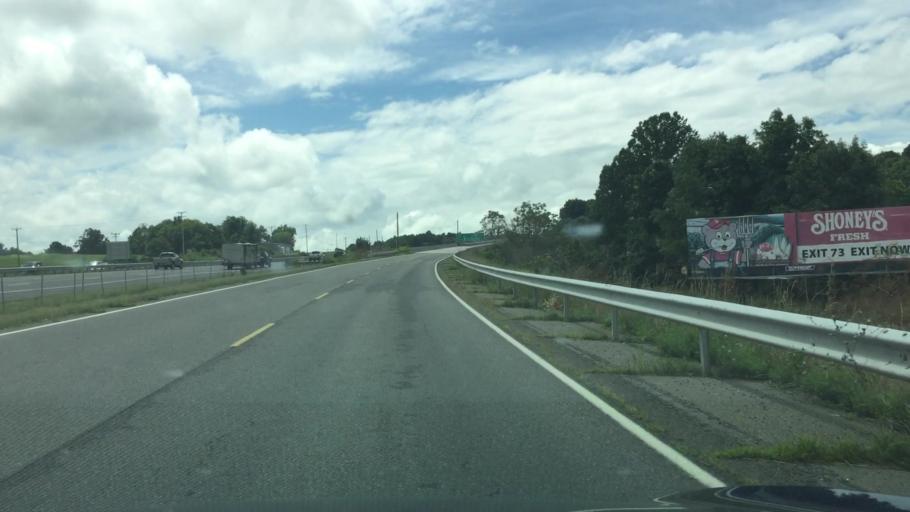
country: US
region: Virginia
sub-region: Wythe County
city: Wytheville
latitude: 36.9461
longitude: -81.0430
